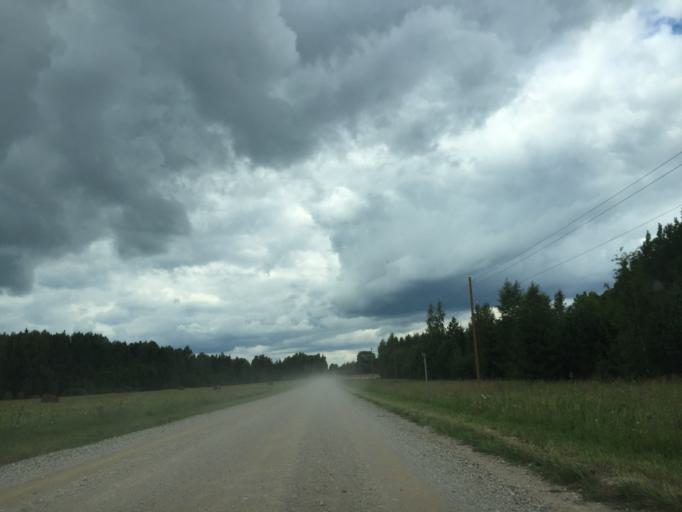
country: LV
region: Malpils
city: Malpils
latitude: 56.8675
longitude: 25.0104
